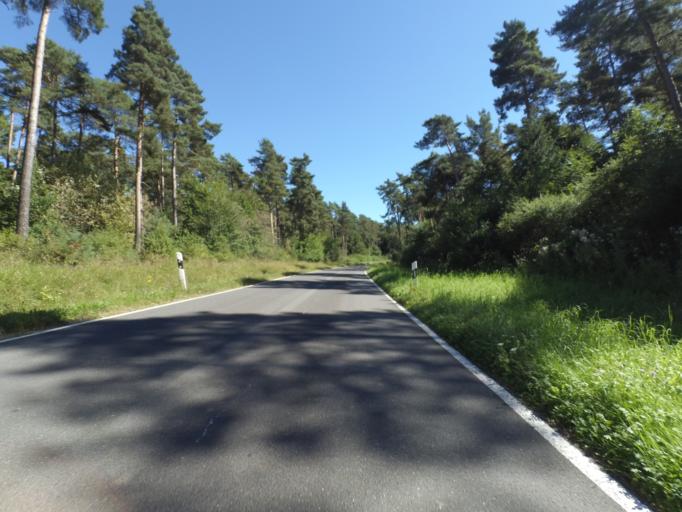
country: DE
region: Rheinland-Pfalz
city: Nohn
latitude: 50.3238
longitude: 6.7583
